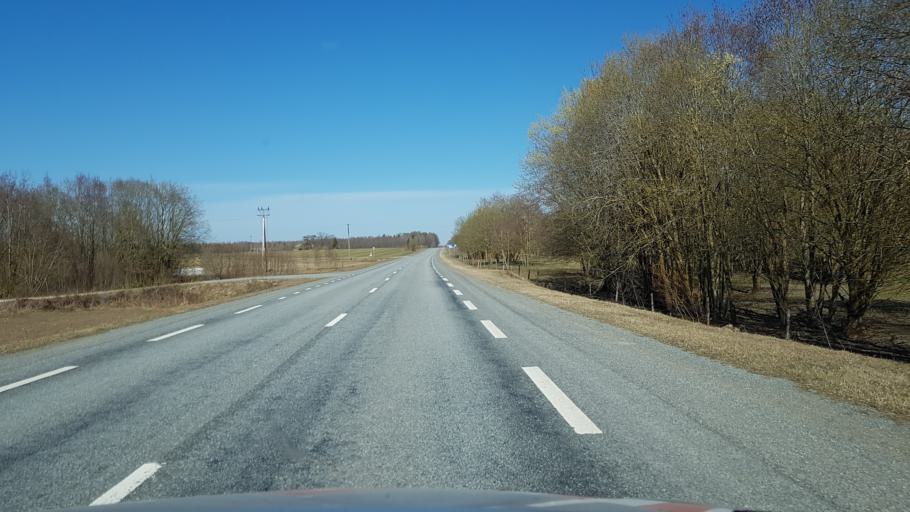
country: EE
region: Jaervamaa
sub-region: Jaerva-Jaani vald
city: Jarva-Jaani
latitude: 59.0802
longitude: 25.9624
